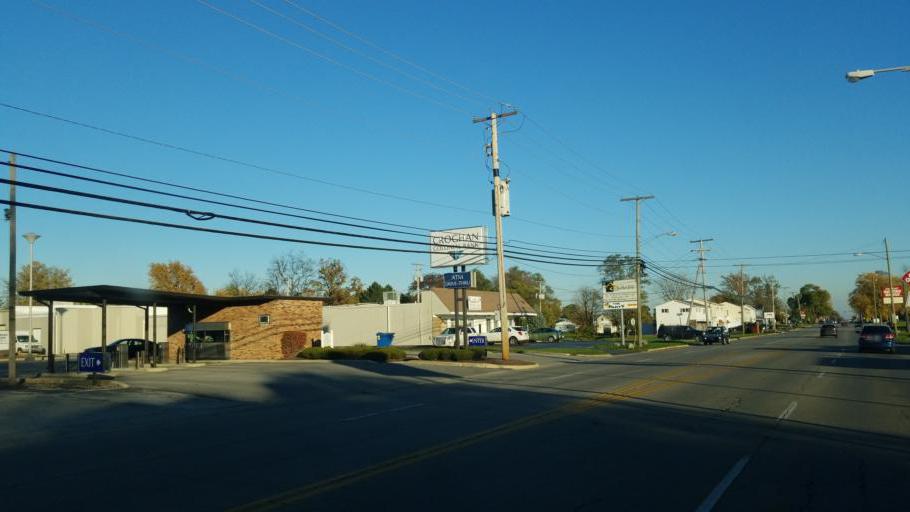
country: US
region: Ohio
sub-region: Sandusky County
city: Fremont
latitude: 41.3425
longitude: -83.0953
